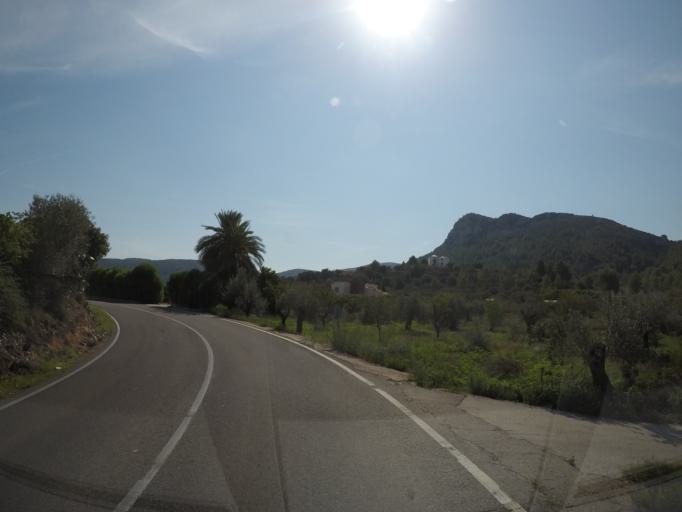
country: ES
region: Valencia
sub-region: Provincia de Alicante
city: Orba
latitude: 38.7802
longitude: -0.0725
